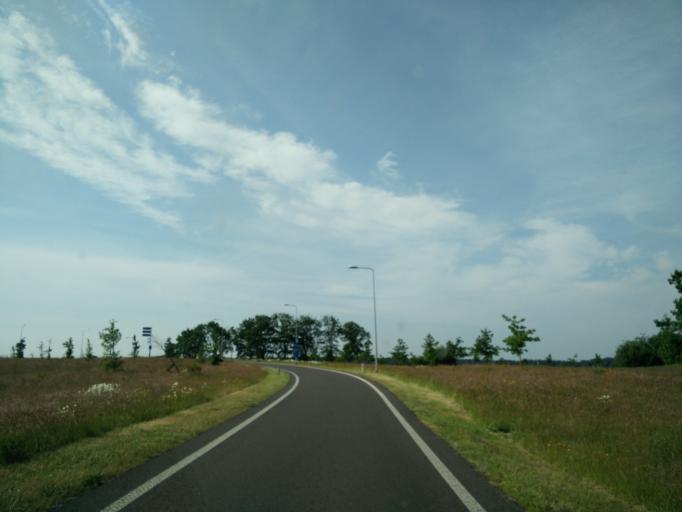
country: NL
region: Drenthe
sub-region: Gemeente Borger-Odoorn
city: Borger
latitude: 52.9757
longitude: 6.7752
